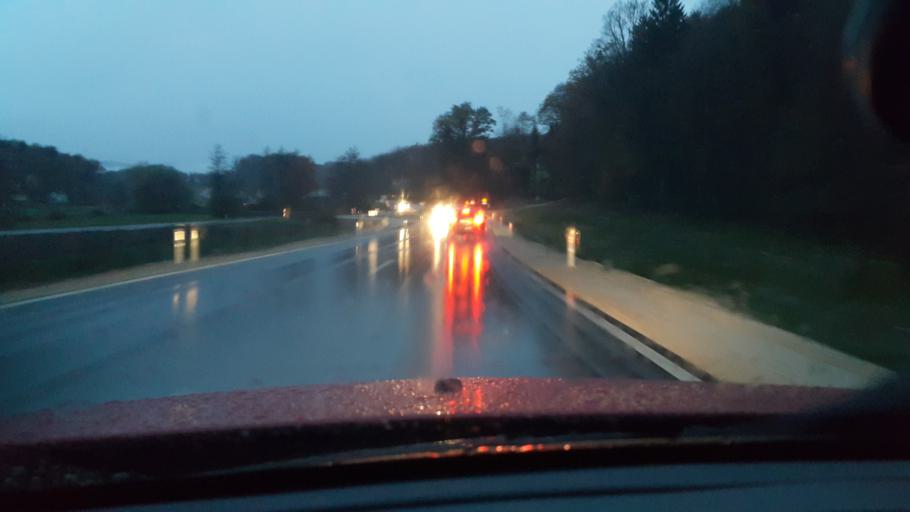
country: SI
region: Poljcane
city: Poljcane
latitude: 46.3294
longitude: 15.5752
